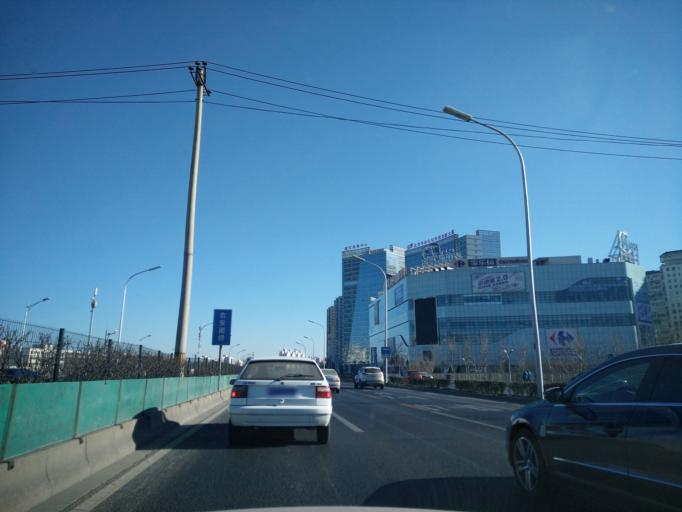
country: CN
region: Beijing
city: Baizhifang
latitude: 39.8533
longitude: 116.3577
